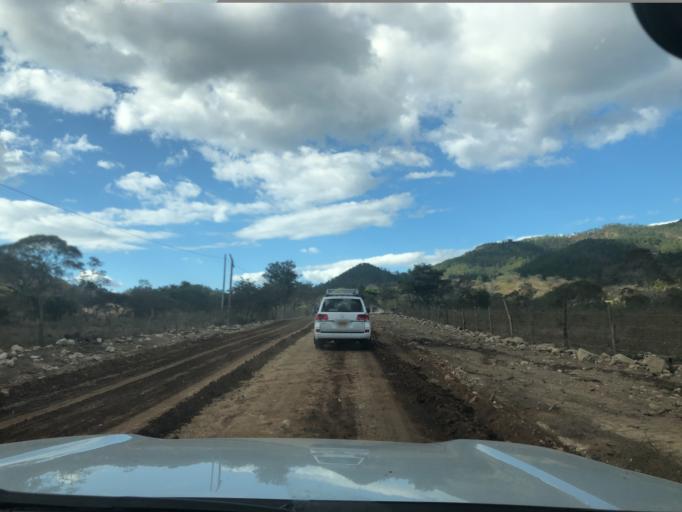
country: NI
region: Nueva Segovia
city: Ocotal
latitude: 13.6624
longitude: -86.6134
